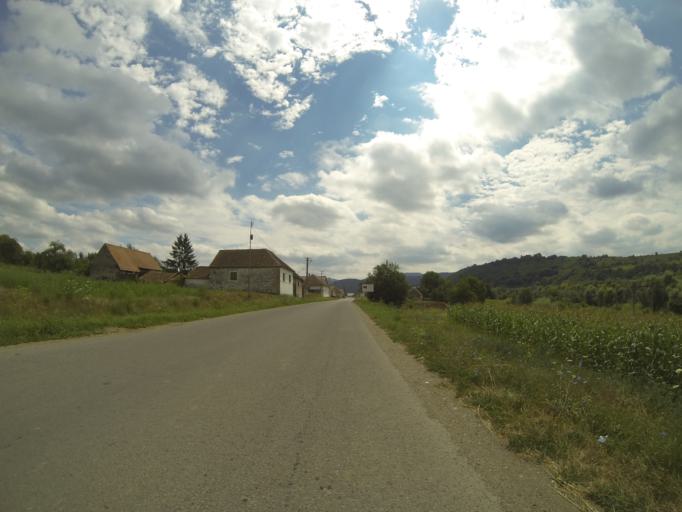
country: RO
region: Brasov
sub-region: Comuna Hoghiz
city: Hoghiz
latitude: 46.0267
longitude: 25.3972
